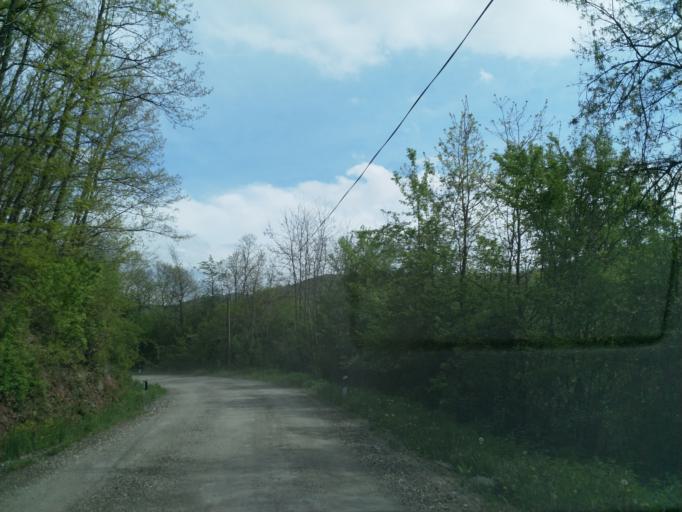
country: RS
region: Central Serbia
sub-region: Pomoravski Okrug
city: Despotovac
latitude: 43.9557
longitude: 21.5705
